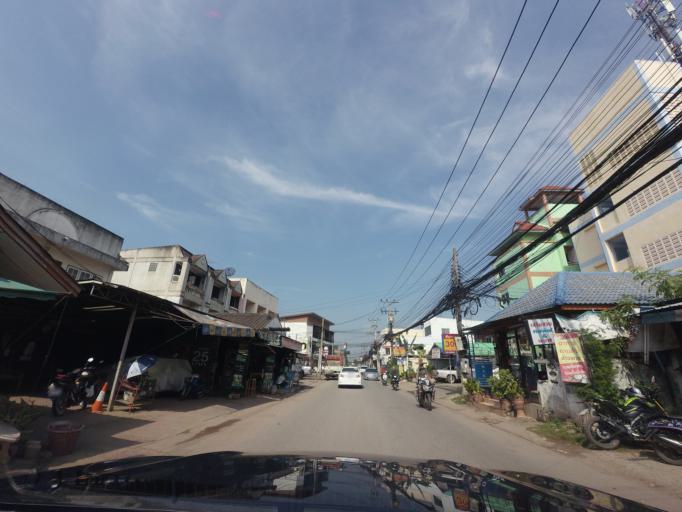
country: TH
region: Khon Kaen
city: Khon Kaen
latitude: 16.4211
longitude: 102.8231
